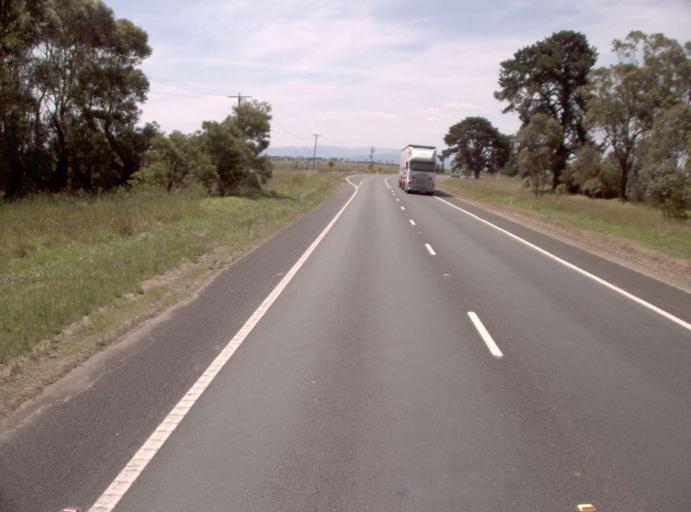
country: AU
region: Victoria
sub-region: Wellington
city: Sale
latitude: -38.0347
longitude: 147.0588
